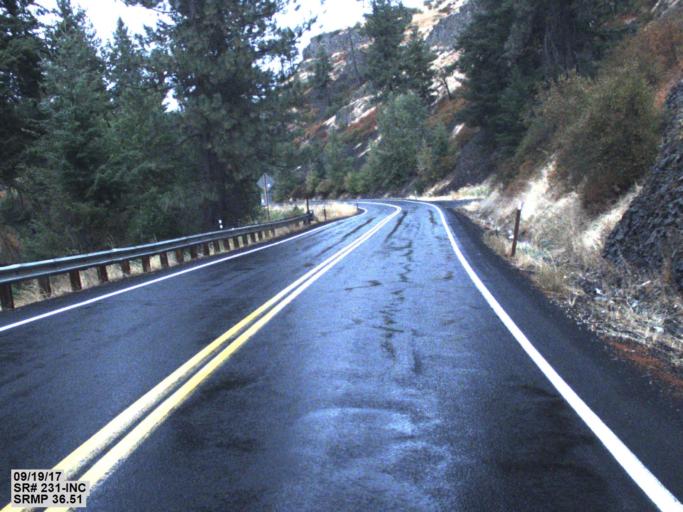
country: US
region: Washington
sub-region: Spokane County
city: Medical Lake
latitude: 47.7413
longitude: -117.8835
